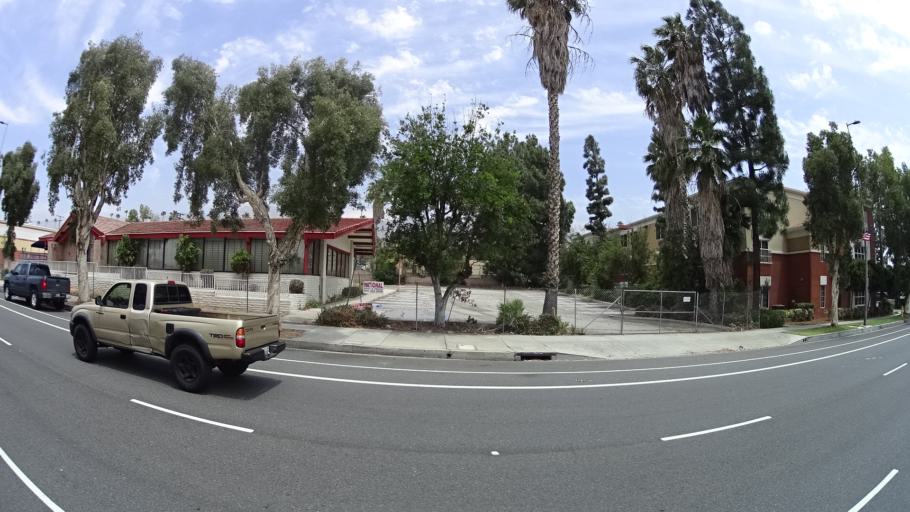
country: US
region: California
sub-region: Los Angeles County
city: North Glendale
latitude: 34.1676
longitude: -118.2848
